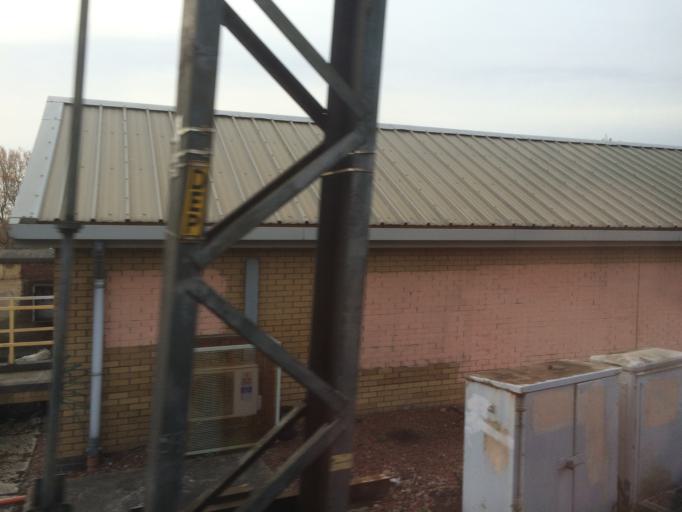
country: GB
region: Scotland
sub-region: Glasgow City
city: Glasgow
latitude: 55.8547
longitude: -4.2591
